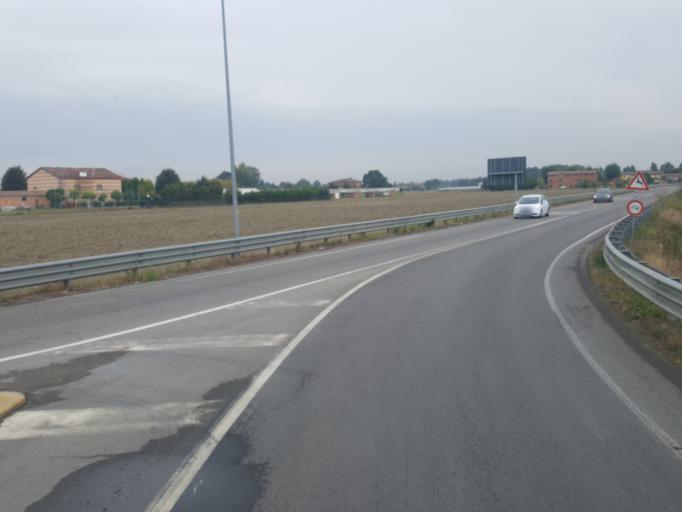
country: IT
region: Emilia-Romagna
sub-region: Provincia di Modena
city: Albareto
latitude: 44.6557
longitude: 10.9704
